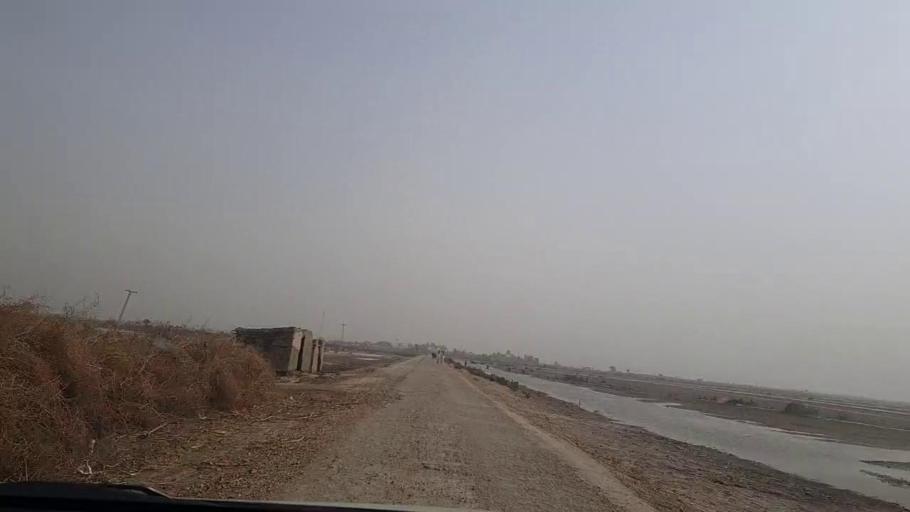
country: PK
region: Sindh
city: Pithoro
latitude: 25.4590
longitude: 69.2304
